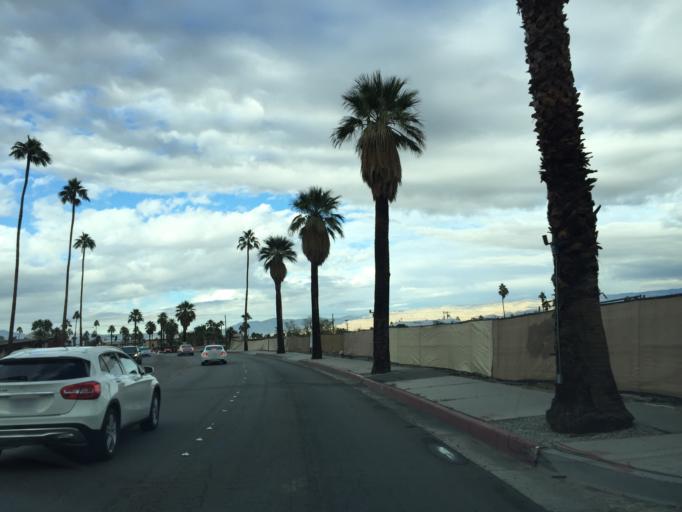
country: US
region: California
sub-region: Riverside County
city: Palm Springs
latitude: 33.8102
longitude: -116.5446
